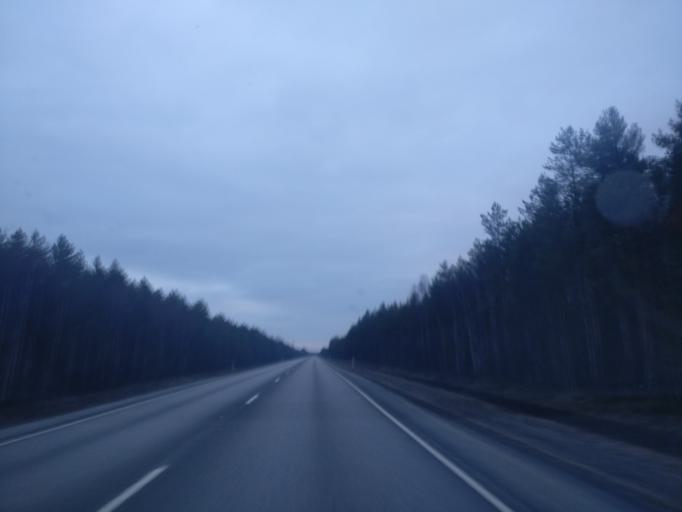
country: FI
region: Northern Ostrobothnia
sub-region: Haapavesi-Siikalatva
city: Rantsila
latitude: 64.5336
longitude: 25.6699
